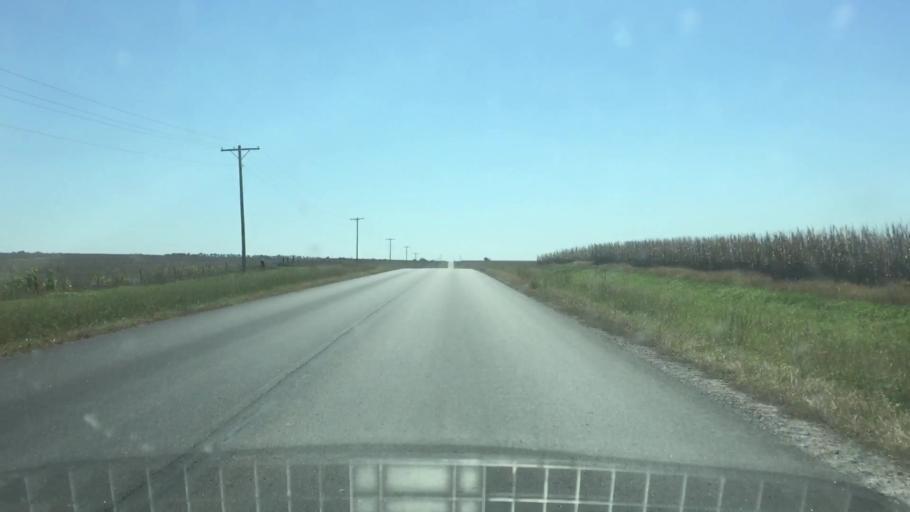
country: US
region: Kansas
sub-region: Marshall County
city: Marysville
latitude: 39.9198
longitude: -96.6009
